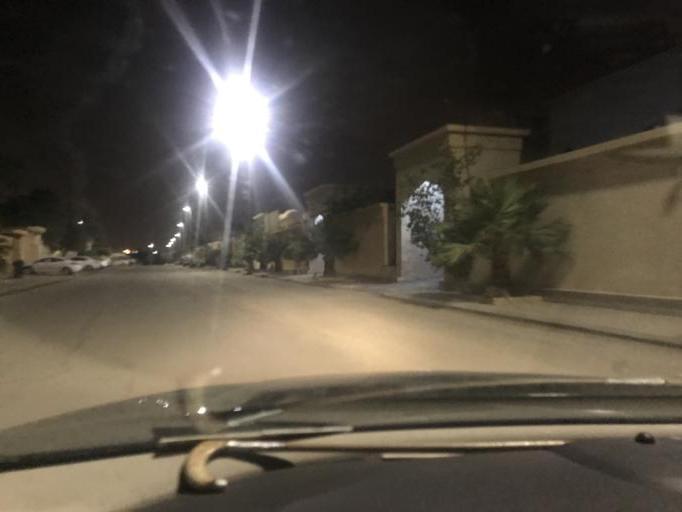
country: SA
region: Ar Riyad
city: Riyadh
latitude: 24.7338
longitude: 46.7800
